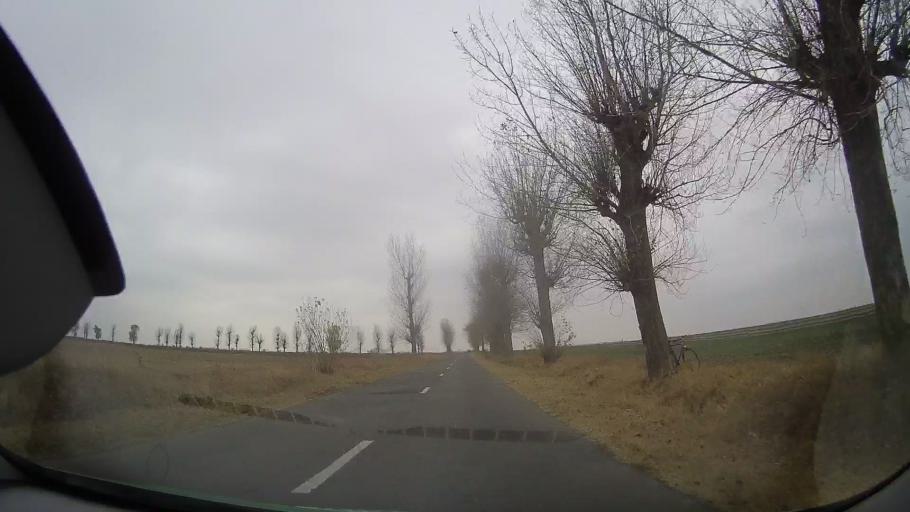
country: RO
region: Ialomita
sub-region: Comuna Grindu
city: Grindu
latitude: 44.7723
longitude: 26.8907
